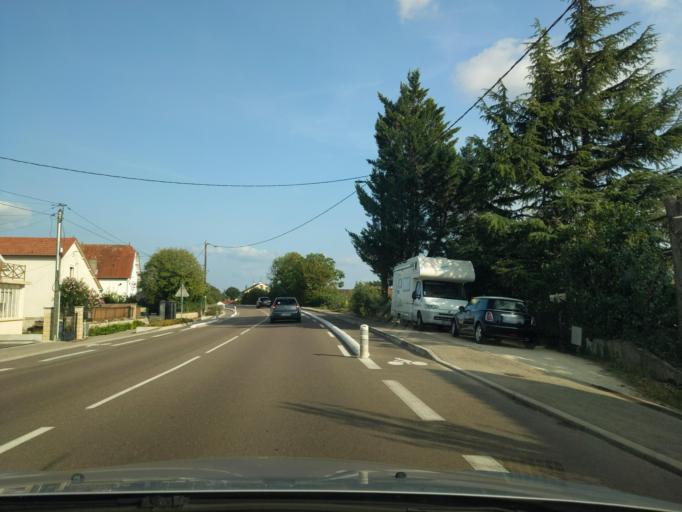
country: FR
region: Bourgogne
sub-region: Departement de la Cote-d'Or
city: Neuilly-les-Dijon
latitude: 47.2818
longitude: 5.1075
